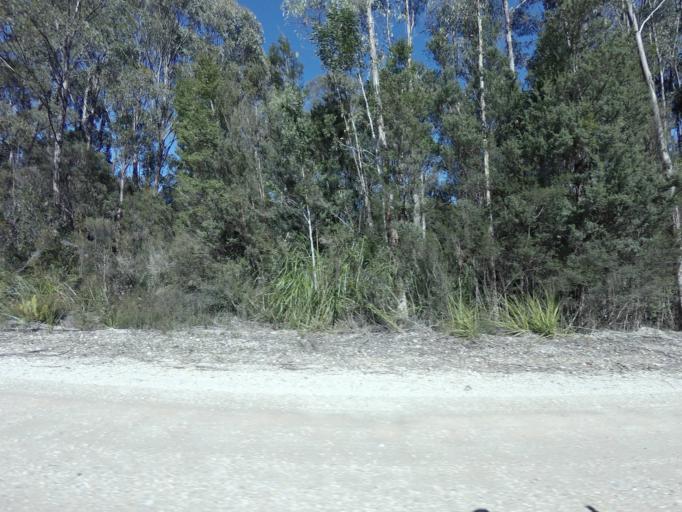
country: AU
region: Tasmania
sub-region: Huon Valley
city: Geeveston
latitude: -42.8744
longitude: 146.3760
